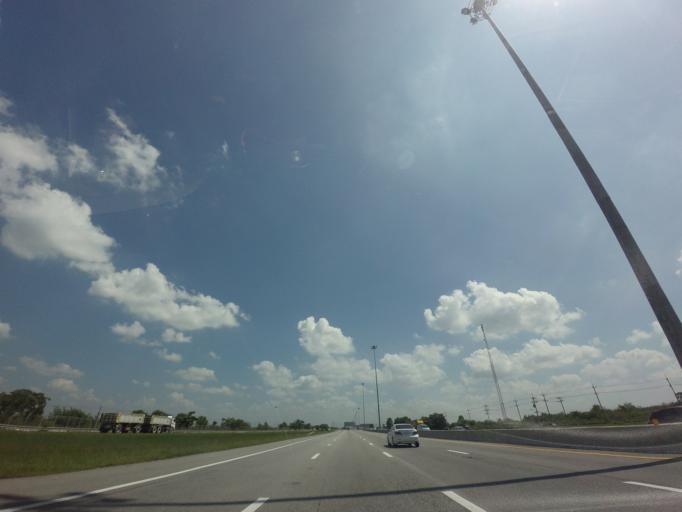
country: TH
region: Chachoengsao
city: Bang Pakong
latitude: 13.5990
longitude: 100.9546
